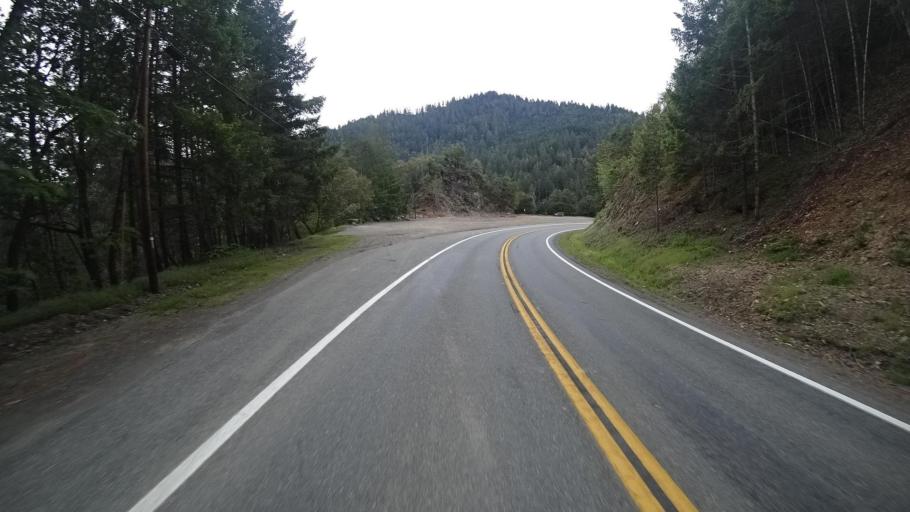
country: US
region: California
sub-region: Humboldt County
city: Willow Creek
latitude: 41.0000
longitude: -123.6262
